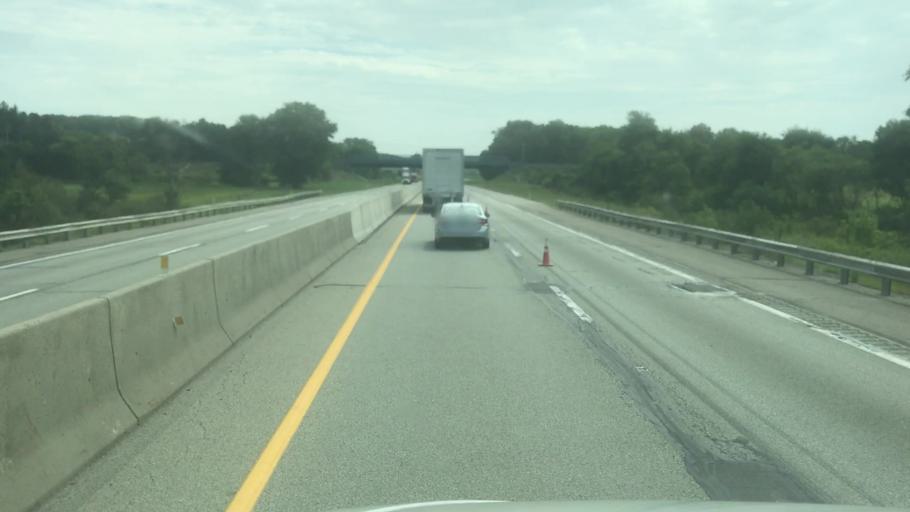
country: US
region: Pennsylvania
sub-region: Butler County
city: Fernway
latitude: 40.7387
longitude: -80.1828
